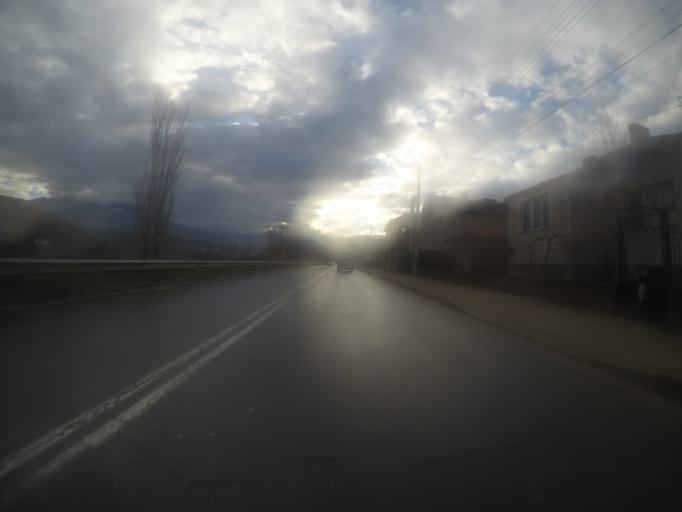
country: BG
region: Blagoevgrad
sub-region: Obshtina Simitli
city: Simitli
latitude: 41.8838
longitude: 23.1206
